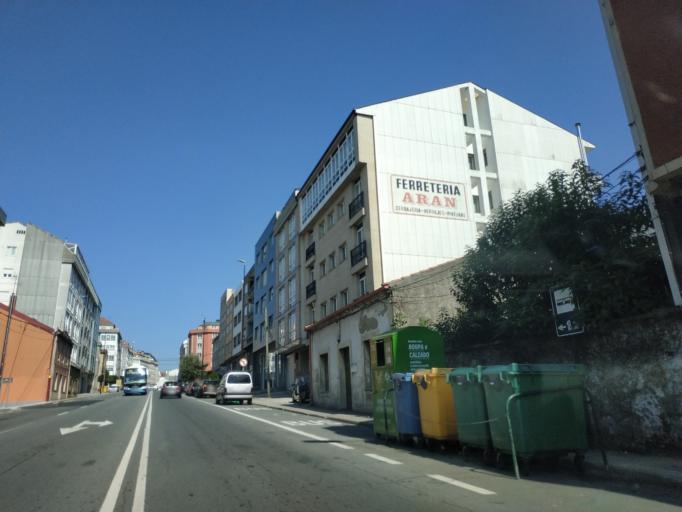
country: ES
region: Galicia
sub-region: Provincia da Coruna
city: Carballo
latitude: 43.2179
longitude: -8.6881
